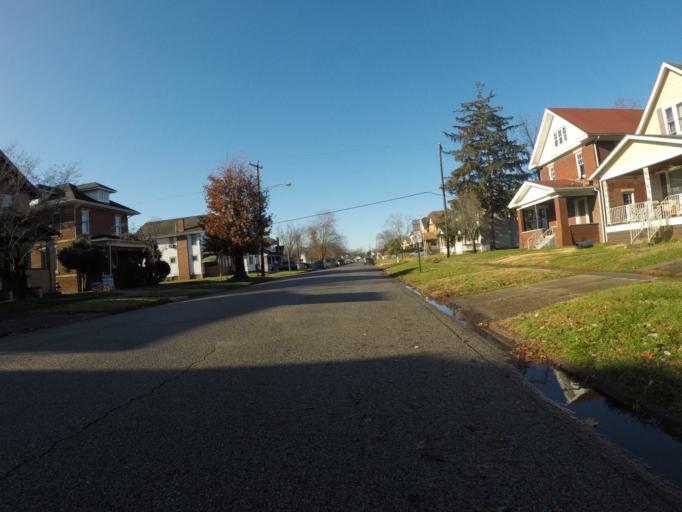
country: US
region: Ohio
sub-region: Lawrence County
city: Burlington
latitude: 38.4100
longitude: -82.4913
